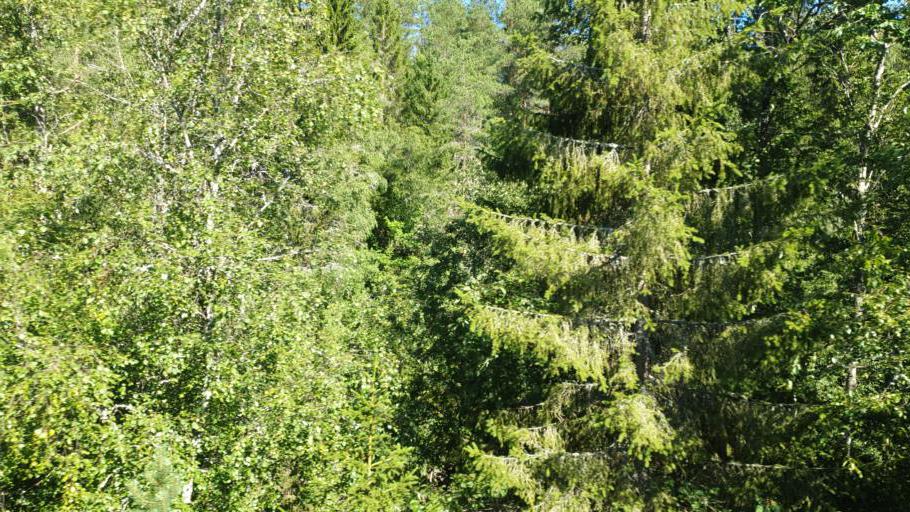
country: NO
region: Sor-Trondelag
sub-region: Meldal
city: Meldal
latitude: 63.1710
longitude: 9.7489
